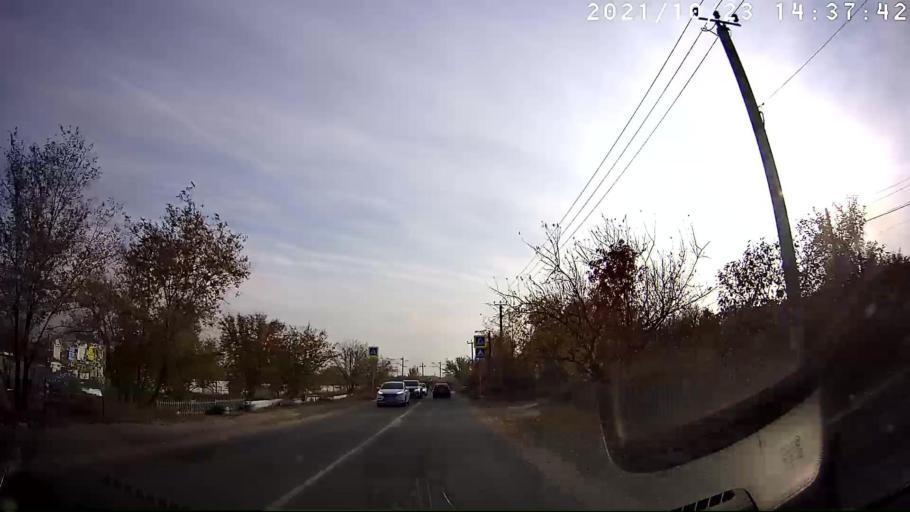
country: RU
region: Volgograd
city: Krasnoslobodsk
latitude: 48.4960
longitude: 44.5496
